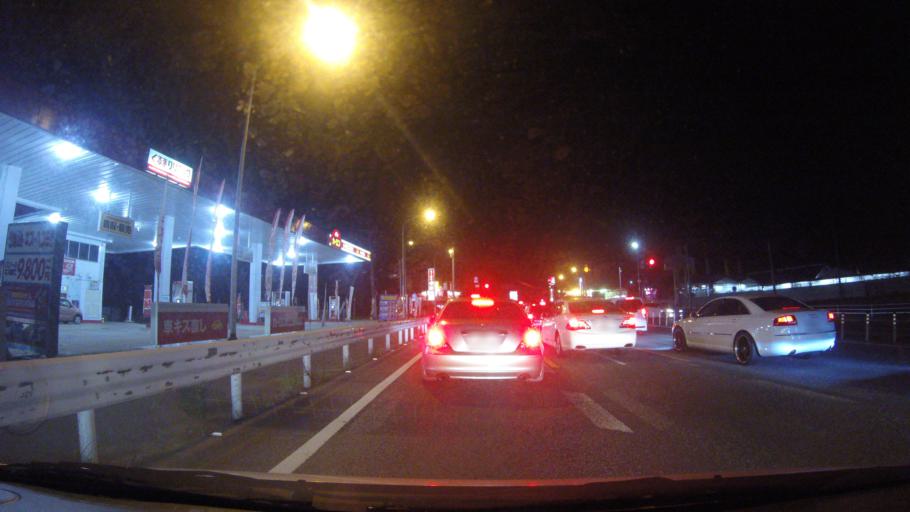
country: JP
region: Fukuoka
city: Shingu
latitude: 33.6851
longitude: 130.4543
